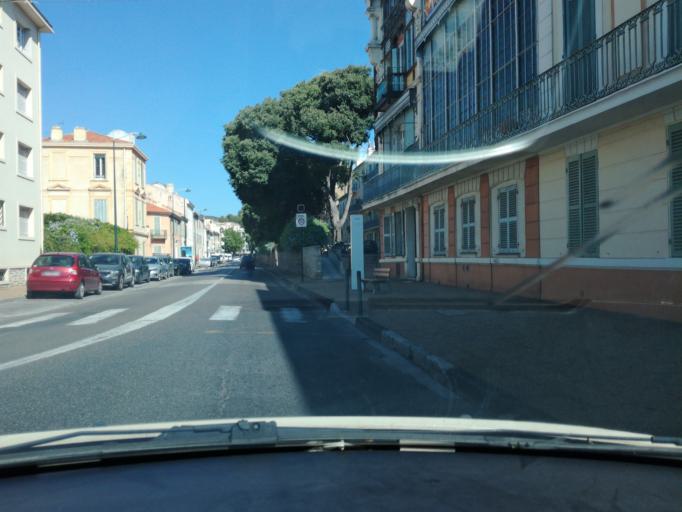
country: FR
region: Provence-Alpes-Cote d'Azur
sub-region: Departement du Var
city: Hyeres
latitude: 43.1201
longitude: 6.1219
